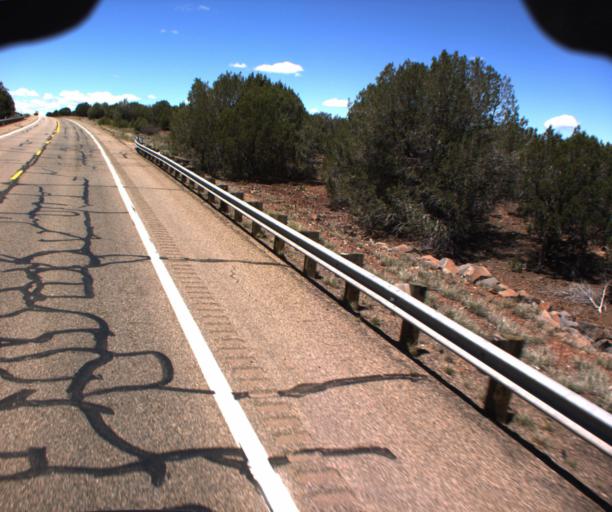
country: US
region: Arizona
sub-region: Yavapai County
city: Paulden
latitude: 35.0857
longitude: -112.4087
